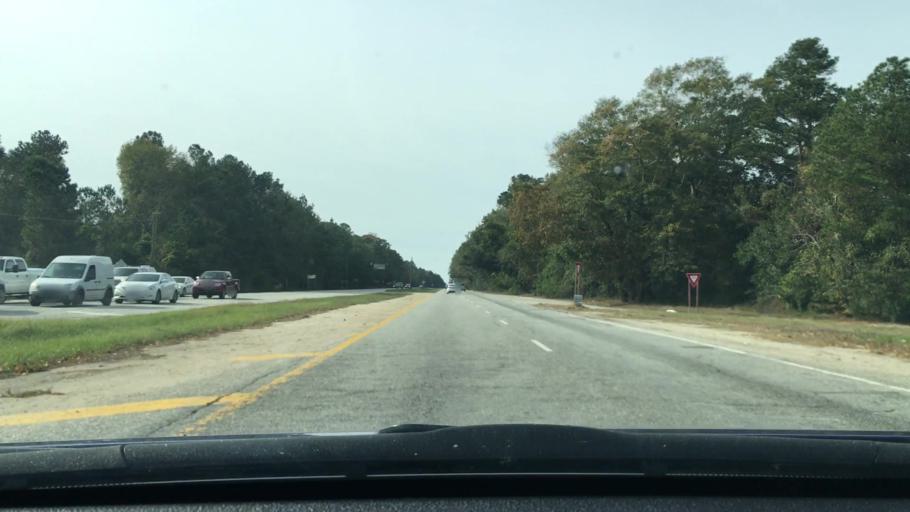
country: US
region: South Carolina
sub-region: Sumter County
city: Stateburg
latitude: 33.9455
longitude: -80.5244
